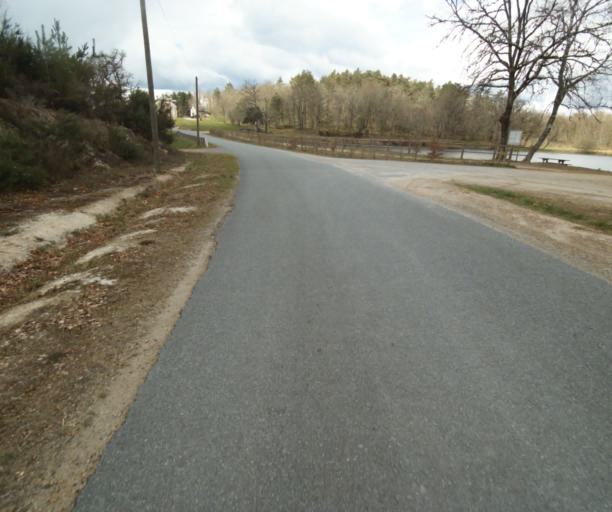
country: FR
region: Limousin
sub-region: Departement de la Correze
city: Correze
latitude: 45.3106
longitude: 1.9332
